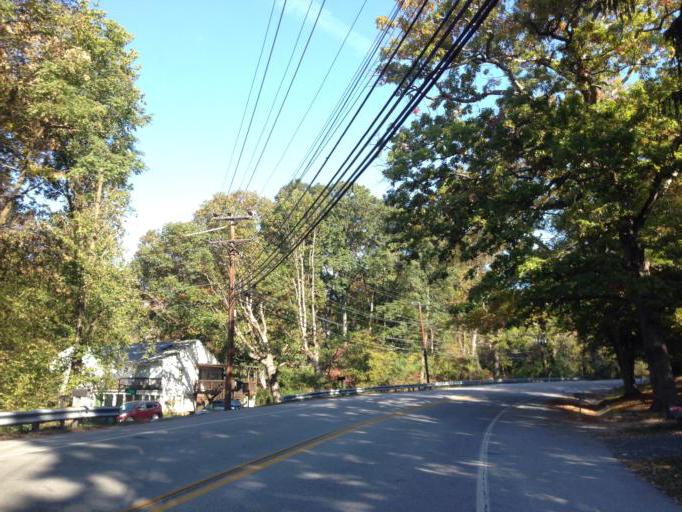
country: US
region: Maryland
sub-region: Howard County
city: Ellicott City
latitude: 39.2745
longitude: -76.8100
